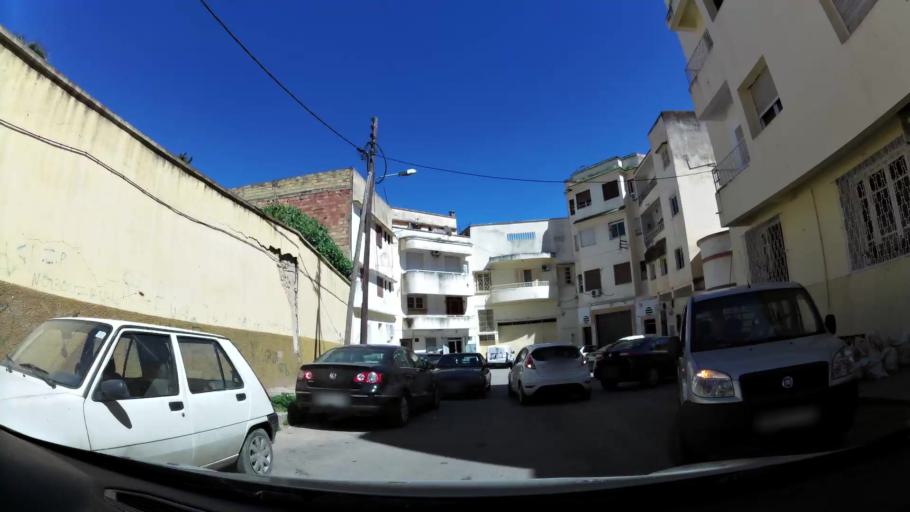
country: MA
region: Meknes-Tafilalet
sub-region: Meknes
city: Meknes
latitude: 33.8953
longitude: -5.5466
